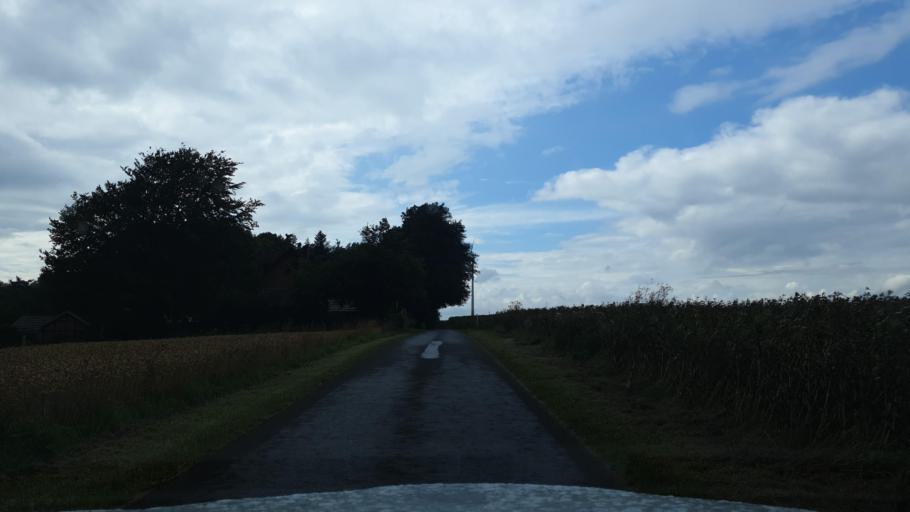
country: DE
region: North Rhine-Westphalia
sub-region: Regierungsbezirk Detmold
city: Bad Salzuflen
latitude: 52.1266
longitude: 8.7550
